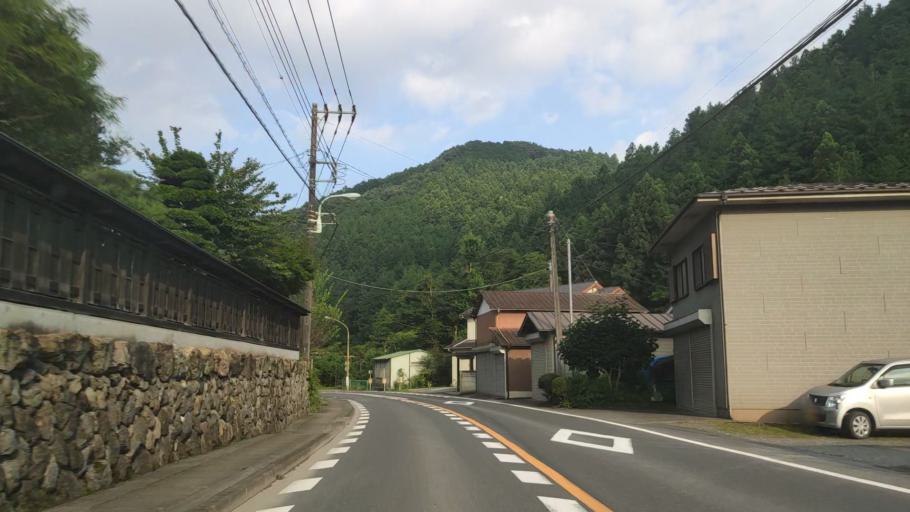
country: JP
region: Tokyo
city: Ome
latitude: 35.8230
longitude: 139.2505
